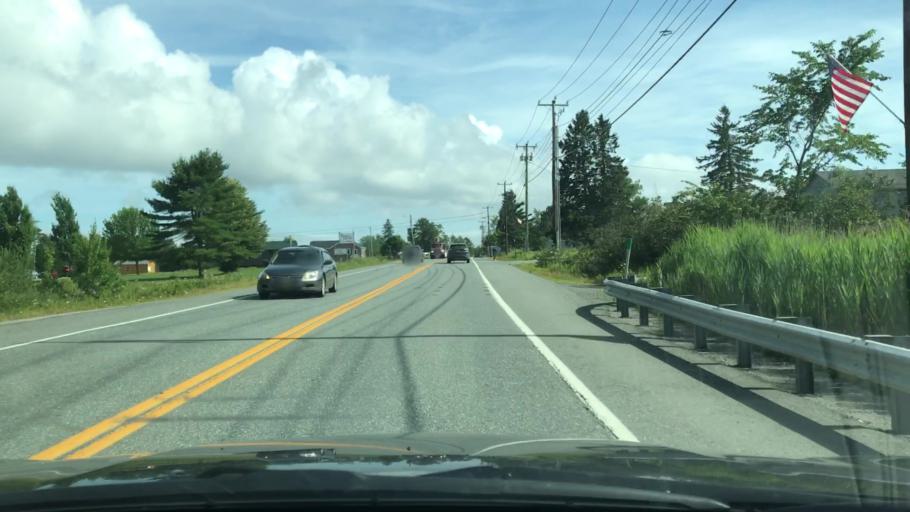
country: US
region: Maine
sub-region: Hancock County
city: Trenton
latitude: 44.4680
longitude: -68.3627
